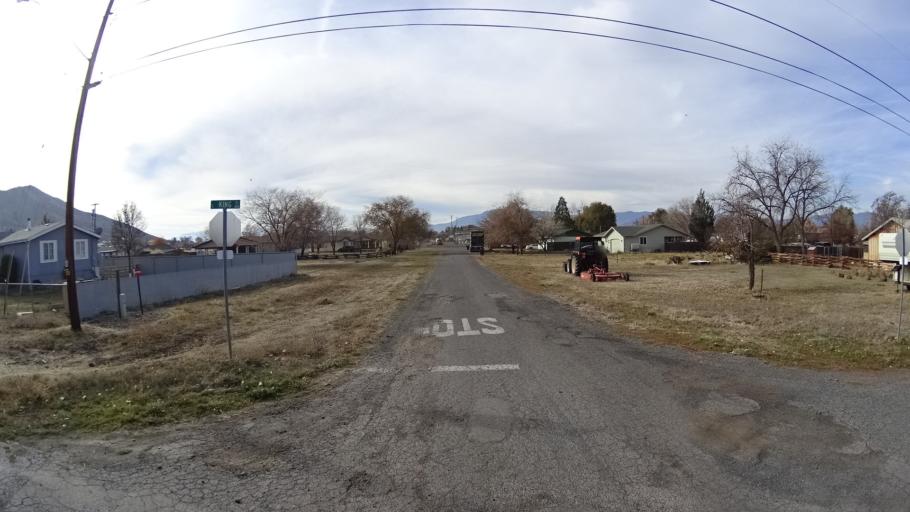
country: US
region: California
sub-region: Siskiyou County
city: Montague
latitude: 41.7253
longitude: -122.5242
